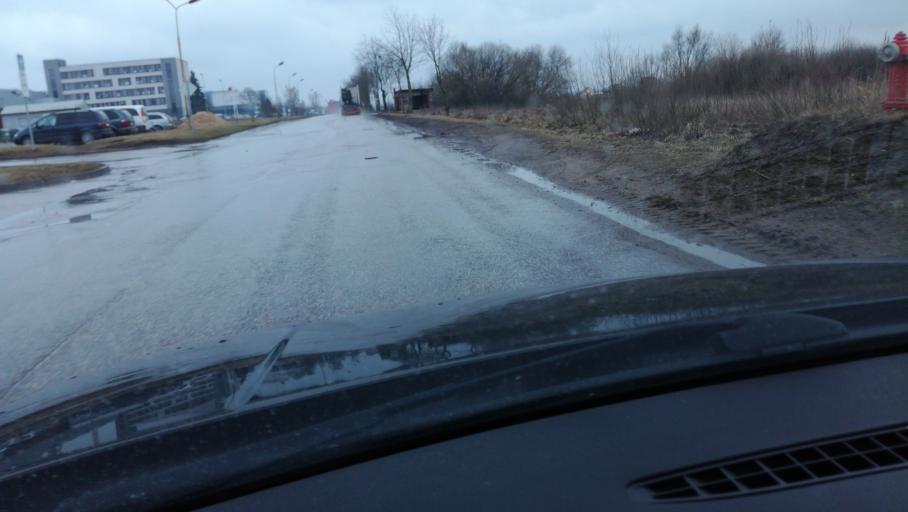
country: LT
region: Alytaus apskritis
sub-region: Alytus
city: Alytus
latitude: 54.4358
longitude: 24.0050
